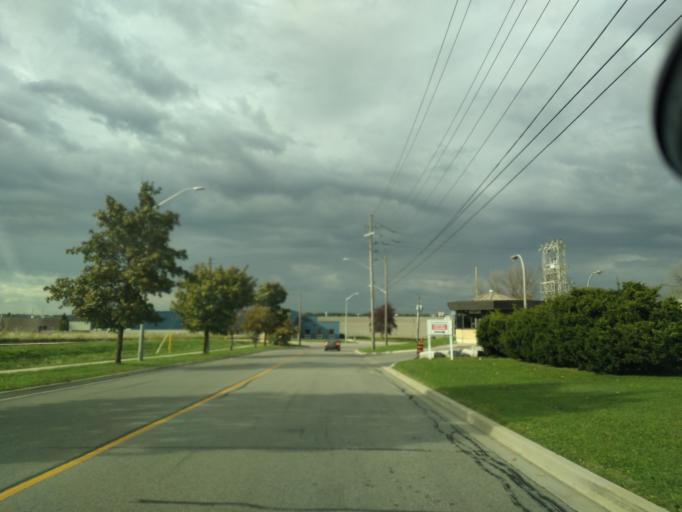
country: CA
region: Ontario
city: Newmarket
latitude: 43.9861
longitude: -79.4500
